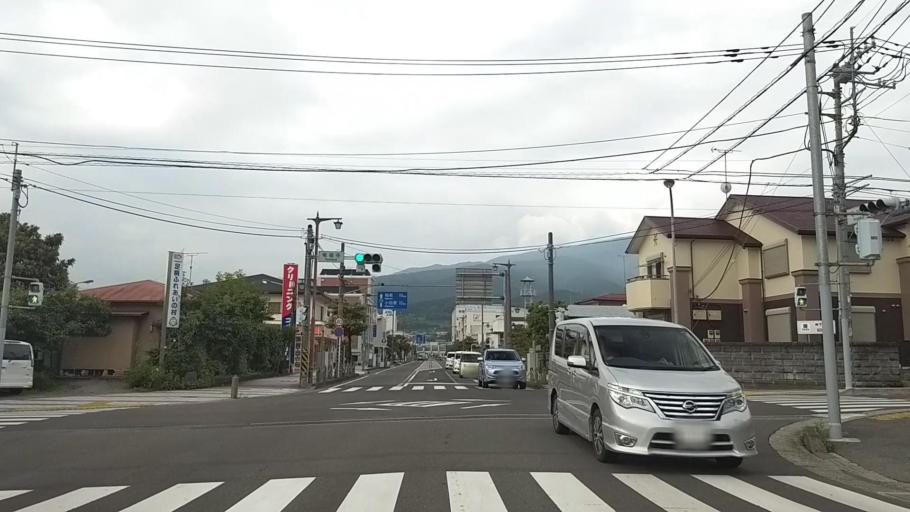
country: JP
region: Kanagawa
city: Odawara
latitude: 35.3216
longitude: 139.1045
